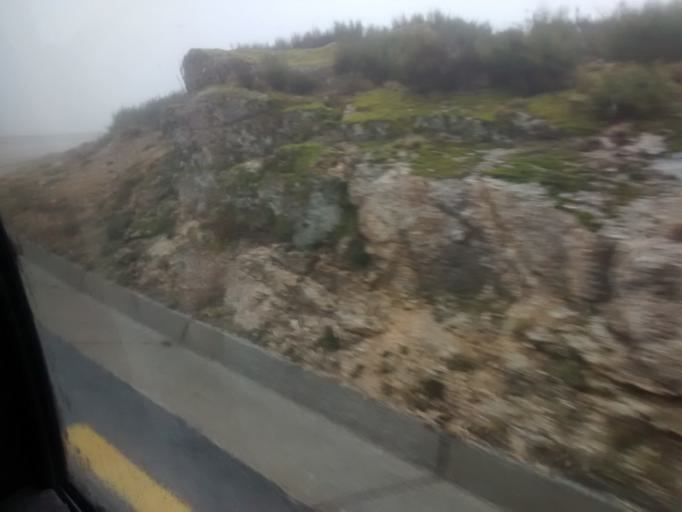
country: PT
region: Guarda
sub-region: Seia
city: Seia
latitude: 40.3910
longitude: -7.6512
